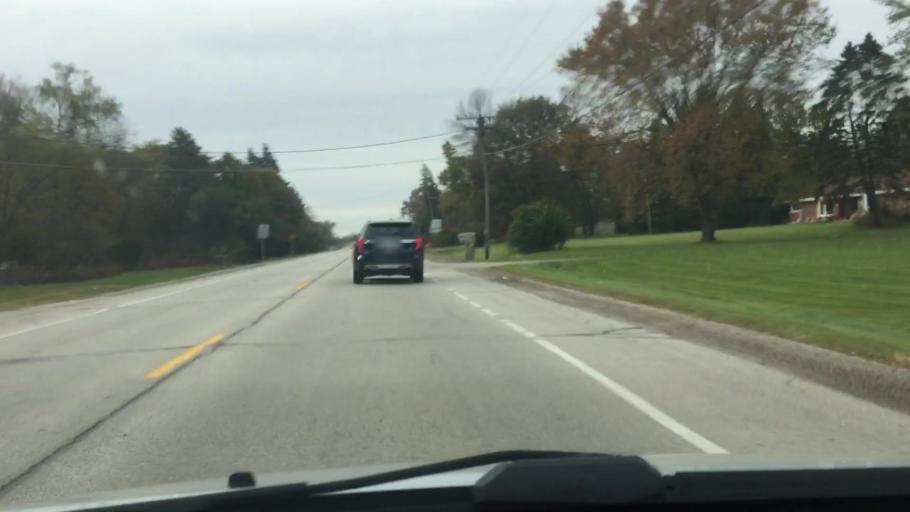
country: US
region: Wisconsin
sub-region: Milwaukee County
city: Franklin
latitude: 42.8959
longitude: -88.0394
